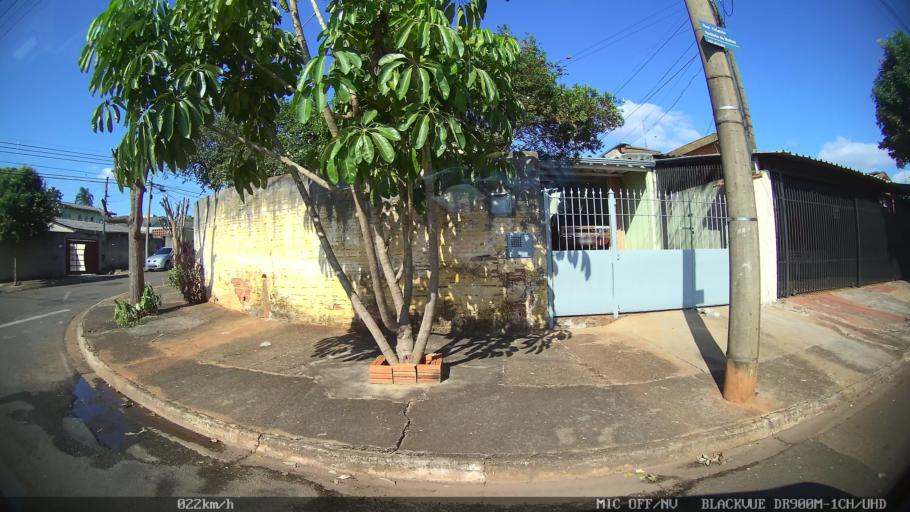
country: BR
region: Sao Paulo
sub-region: Sumare
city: Sumare
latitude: -22.8132
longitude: -47.2904
